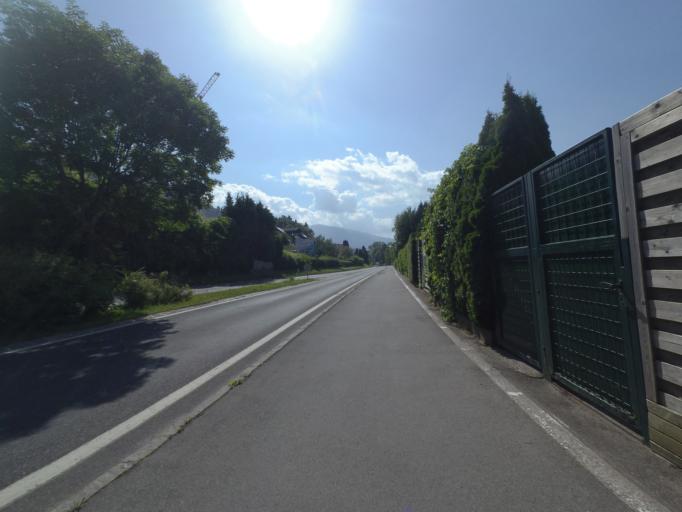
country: AT
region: Carinthia
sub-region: Politischer Bezirk Spittal an der Drau
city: Millstatt
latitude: 46.7970
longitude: 13.5913
